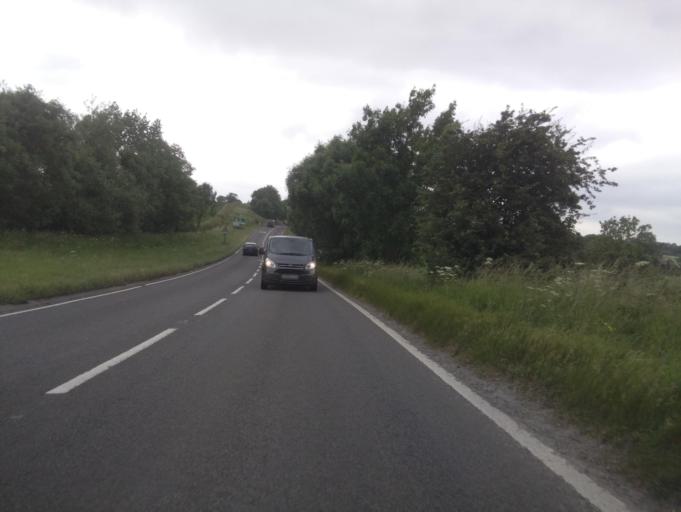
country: GB
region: England
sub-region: Staffordshire
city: Mayfield
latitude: 52.9372
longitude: -1.7619
